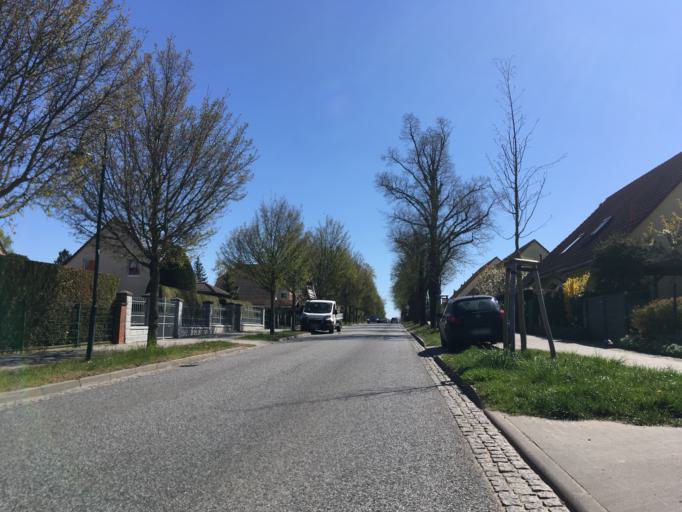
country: DE
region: Brandenburg
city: Bernau bei Berlin
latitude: 52.6492
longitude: 13.5463
